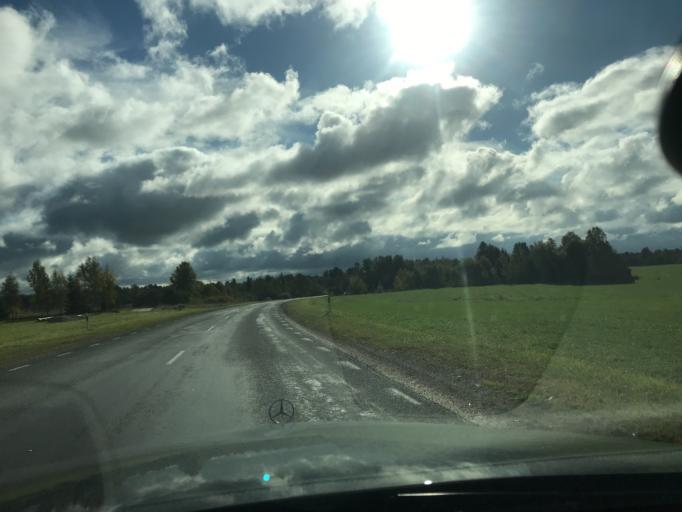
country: EE
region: Tartu
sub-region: Elva linn
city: Elva
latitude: 58.0063
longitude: 26.2627
